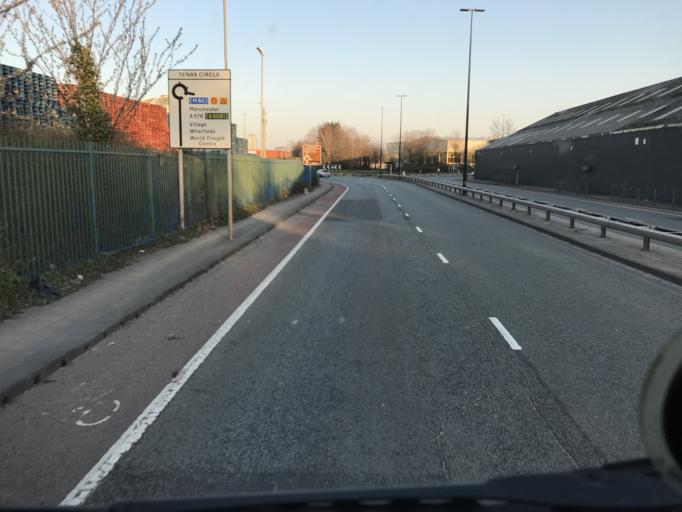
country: GB
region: England
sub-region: City and Borough of Salford
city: Eccles
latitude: 53.4756
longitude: -2.3247
